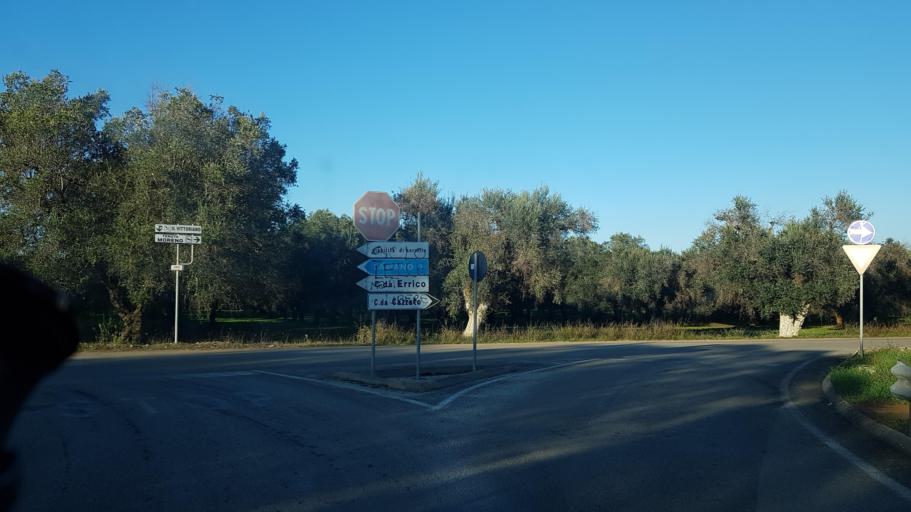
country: IT
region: Apulia
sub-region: Provincia di Brindisi
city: Latiano
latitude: 40.5633
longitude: 17.7366
